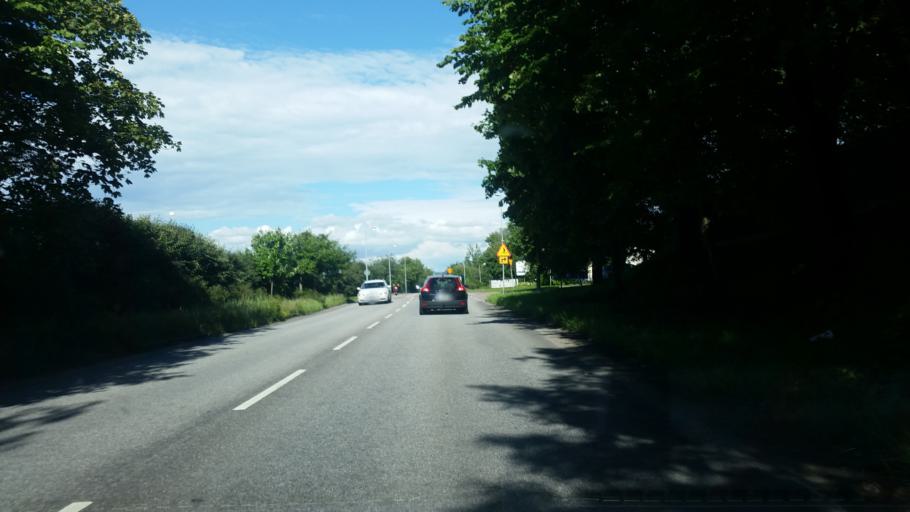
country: SE
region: Vaestra Goetaland
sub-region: Goteborg
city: Eriksbo
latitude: 57.7301
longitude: 12.0539
